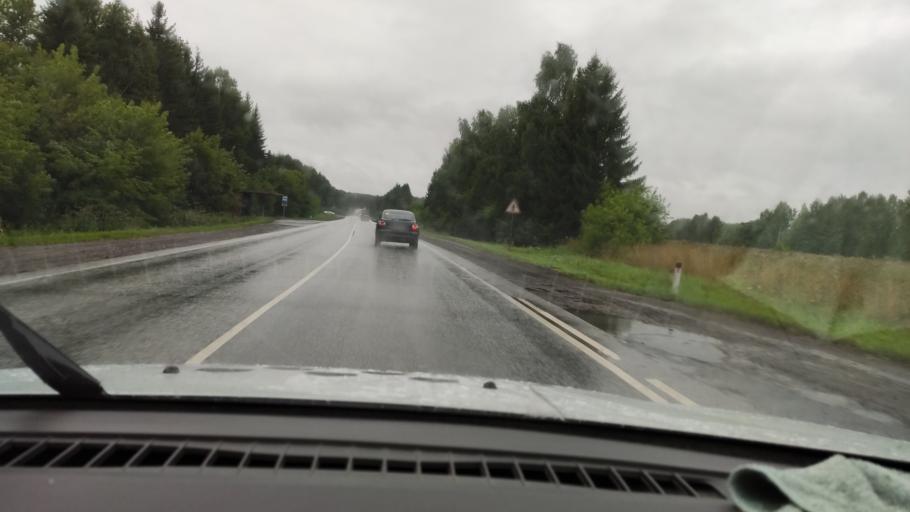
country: RU
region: Perm
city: Kungur
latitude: 57.4524
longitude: 56.7902
